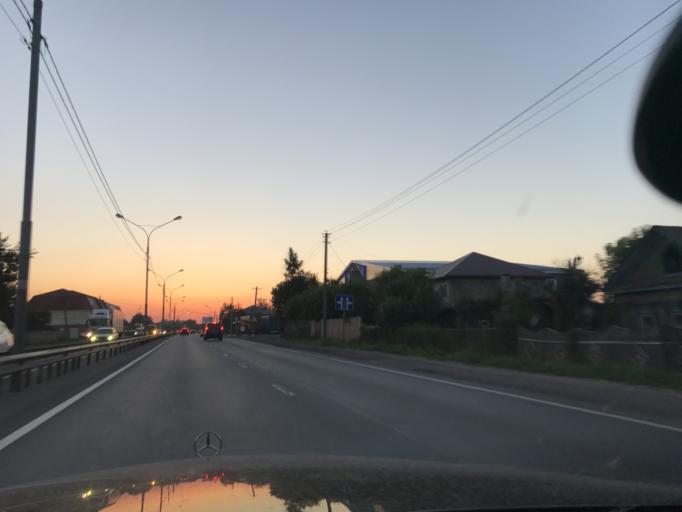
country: RU
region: Moskovskaya
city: Pavlovskiy Posad
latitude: 55.8498
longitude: 38.6644
